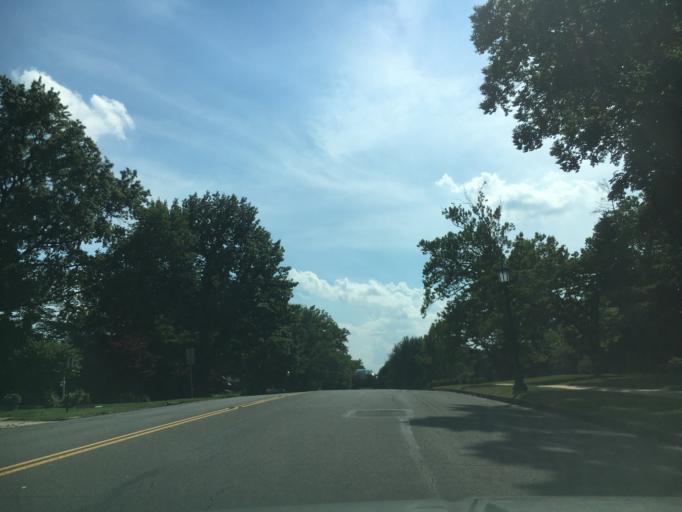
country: US
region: Pennsylvania
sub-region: Berks County
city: West Reading
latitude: 40.3236
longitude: -75.9544
